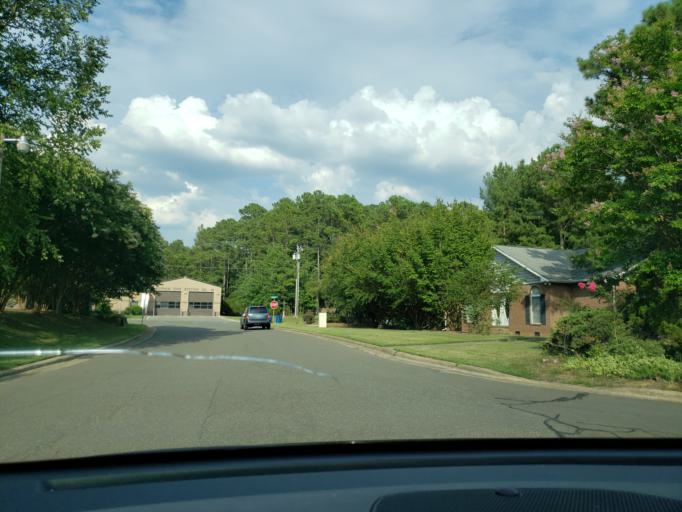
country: US
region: North Carolina
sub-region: Orange County
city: Chapel Hill
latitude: 35.9053
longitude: -78.9838
